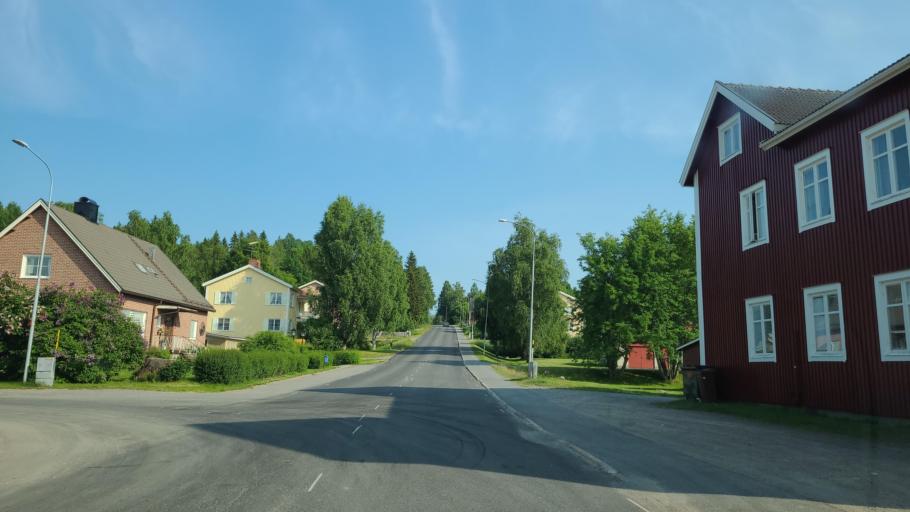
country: SE
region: Vaesterbotten
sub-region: Skelleftea Kommun
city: Burea
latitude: 64.3681
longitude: 21.3217
